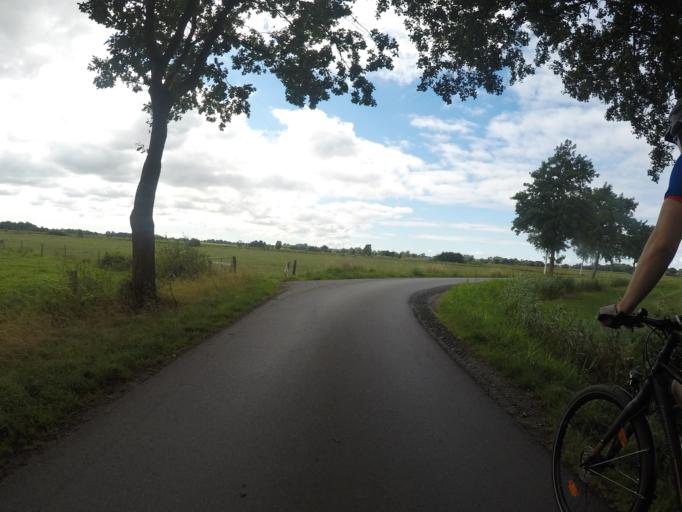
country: DE
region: Lower Saxony
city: Cadenberge
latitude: 53.7580
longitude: 9.0311
